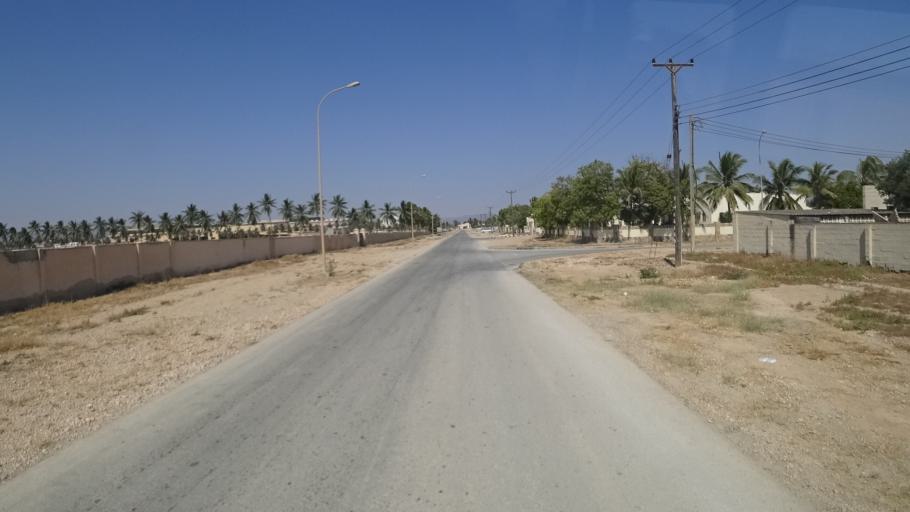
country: OM
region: Zufar
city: Salalah
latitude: 17.0291
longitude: 54.1666
